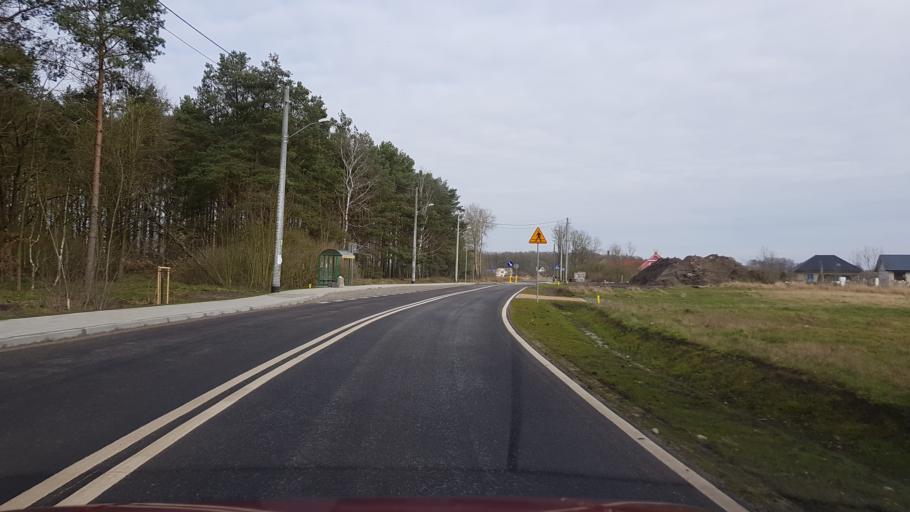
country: PL
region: West Pomeranian Voivodeship
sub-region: Powiat policki
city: Nowe Warpno
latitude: 53.6902
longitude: 14.3551
